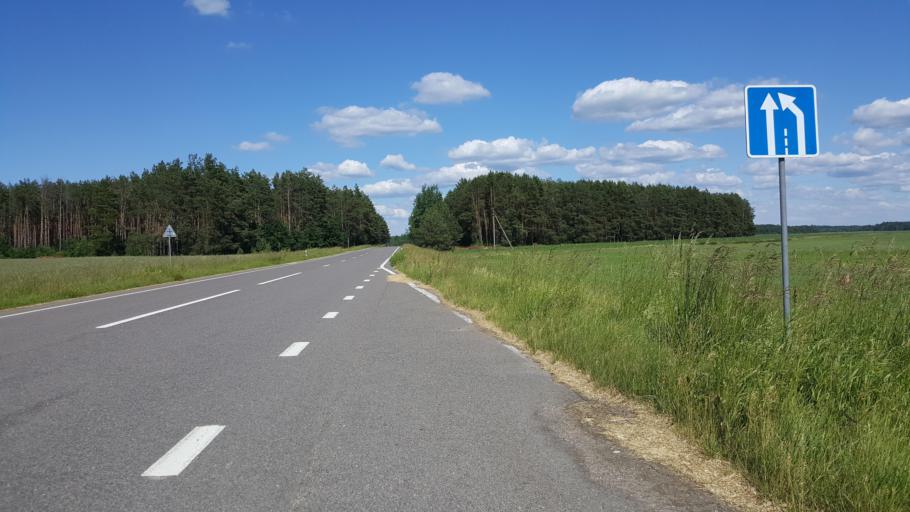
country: PL
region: Podlasie
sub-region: Powiat hajnowski
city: Hajnowka
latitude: 52.5546
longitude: 23.5935
